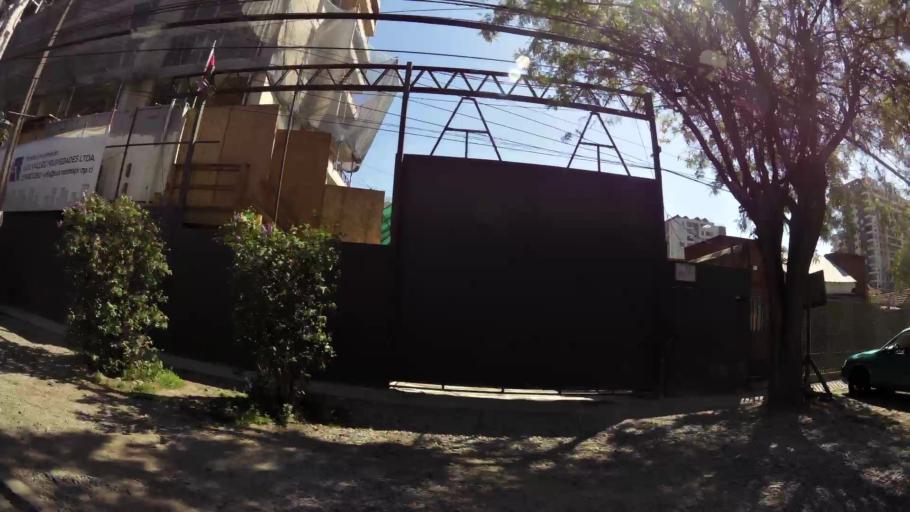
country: CL
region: Santiago Metropolitan
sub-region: Provincia de Santiago
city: Santiago
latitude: -33.5089
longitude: -70.6542
